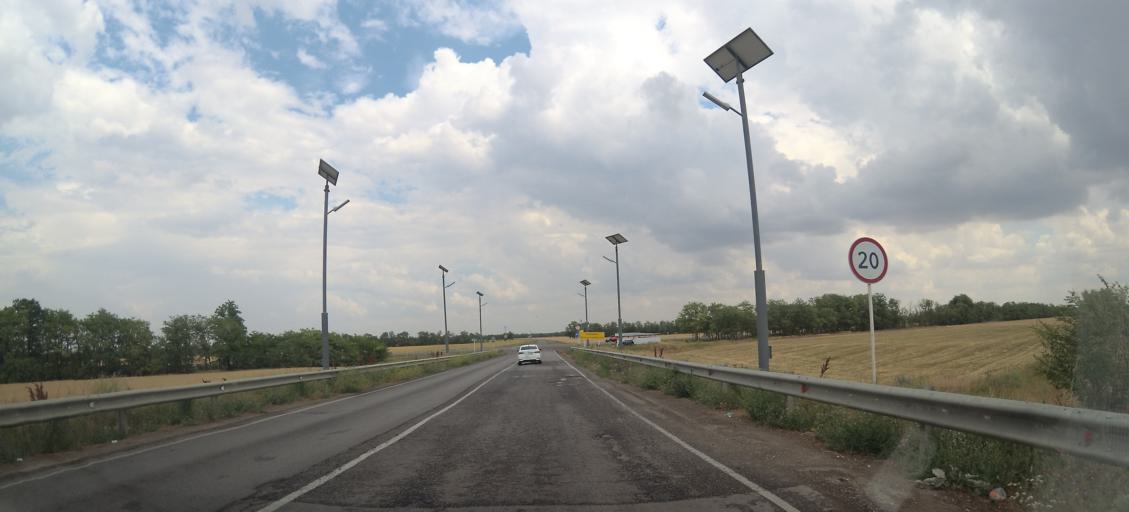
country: RU
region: Rostov
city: Letnik
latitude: 46.0869
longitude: 41.1868
